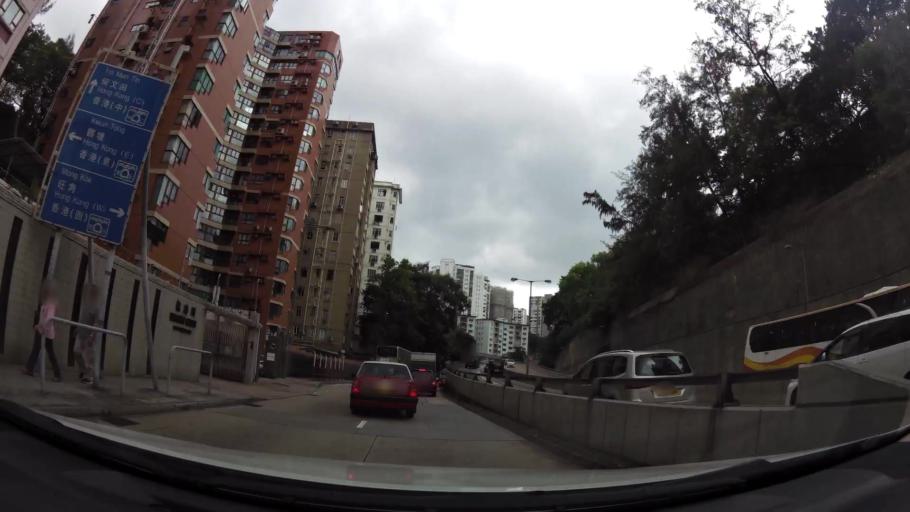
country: HK
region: Kowloon City
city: Kowloon
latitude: 22.3232
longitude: 114.1784
